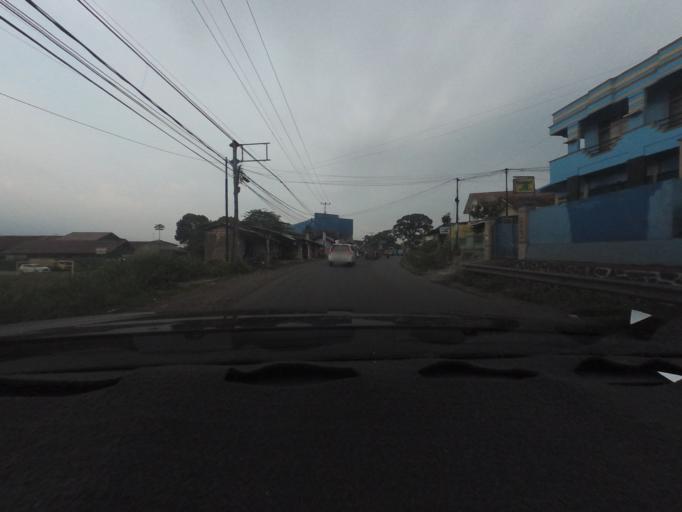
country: ID
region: West Java
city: Cicurug
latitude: -6.7983
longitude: 106.7762
